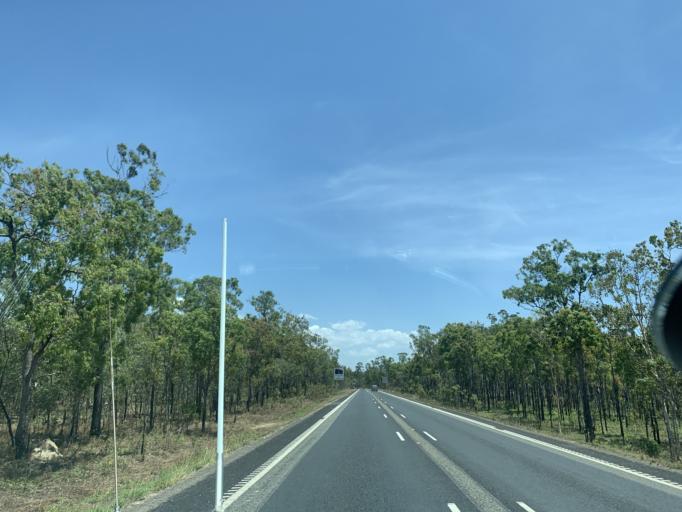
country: AU
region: Queensland
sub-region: Tablelands
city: Mareeba
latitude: -16.9336
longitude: 145.5453
